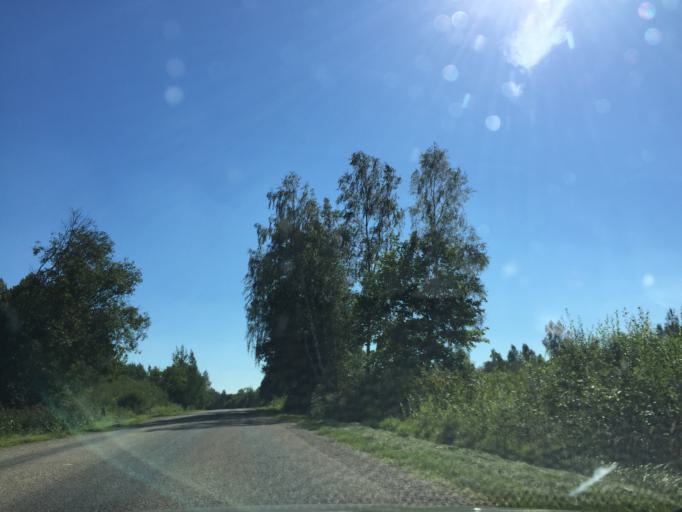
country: LV
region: Akniste
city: Akniste
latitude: 56.0415
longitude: 25.9082
